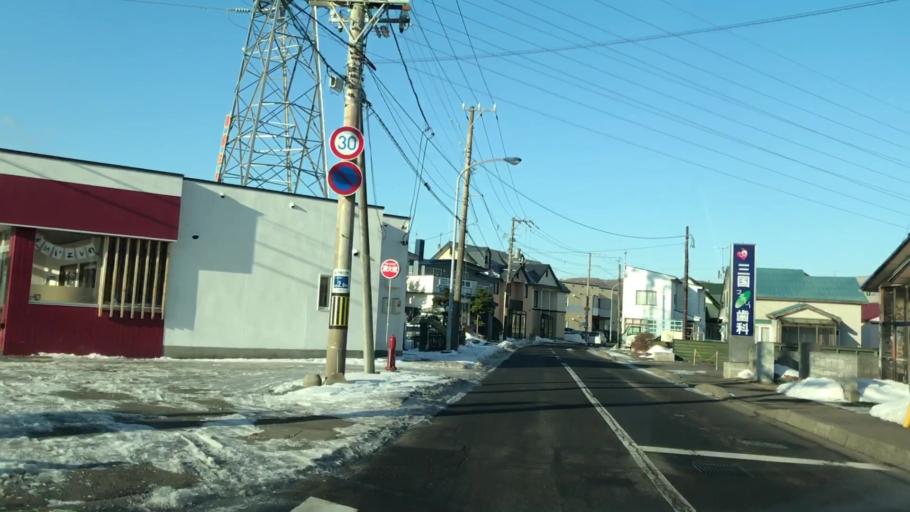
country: JP
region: Hokkaido
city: Muroran
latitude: 42.3635
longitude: 141.0459
